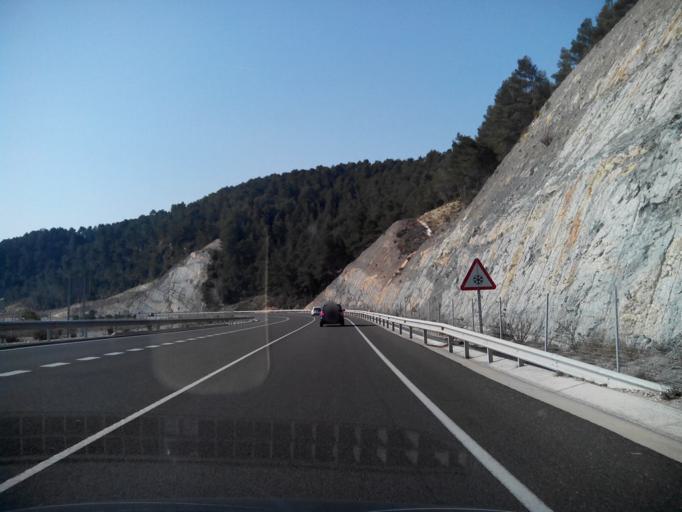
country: ES
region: Catalonia
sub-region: Provincia de Barcelona
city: Castelloli
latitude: 41.6190
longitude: 1.6823
